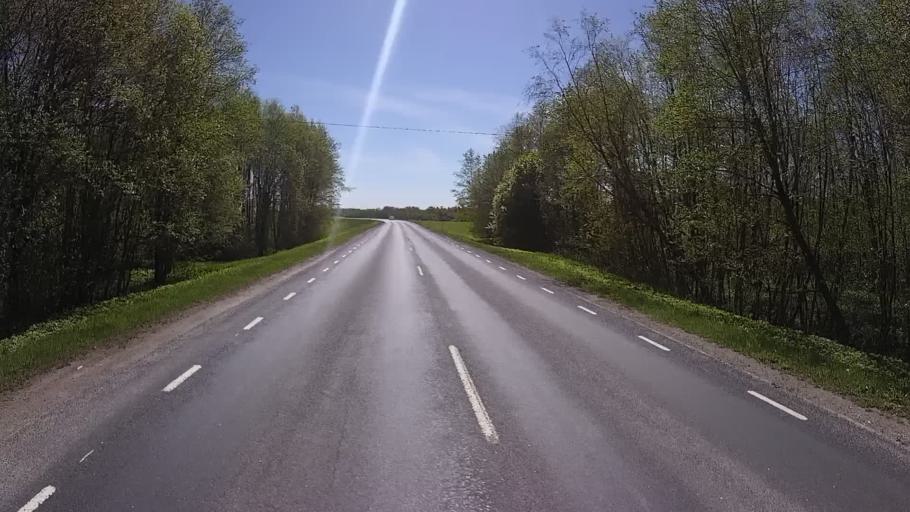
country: EE
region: Harju
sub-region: Raasiku vald
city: Raasiku
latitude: 59.1398
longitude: 25.2018
